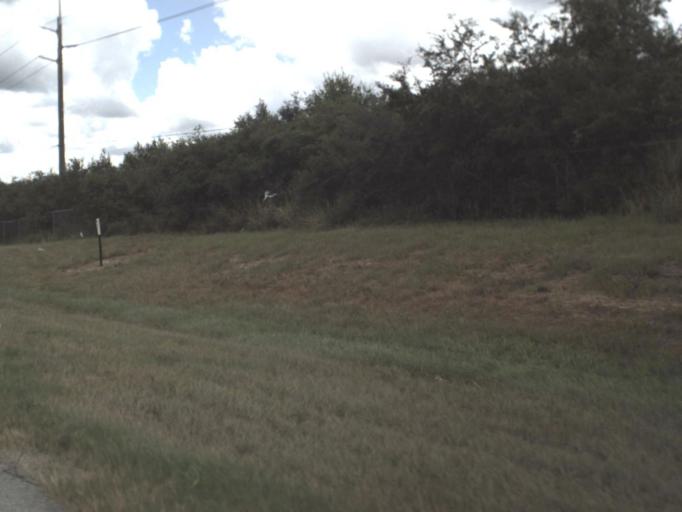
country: US
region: Florida
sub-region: Polk County
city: Mulberry
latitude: 27.8946
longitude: -81.9308
